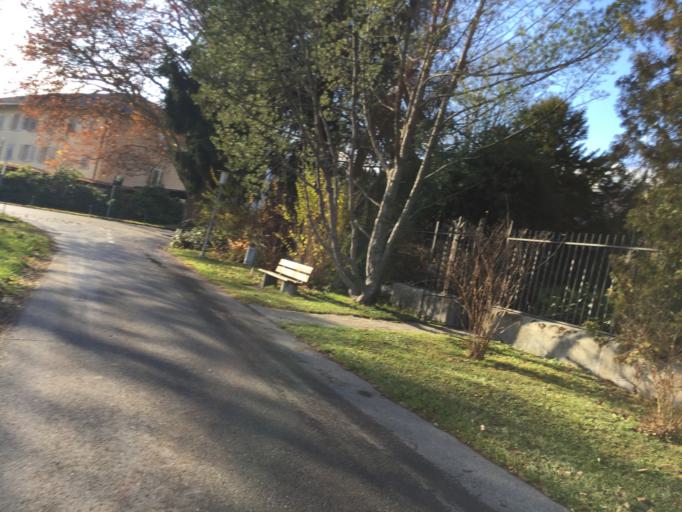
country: CH
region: Bern
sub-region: Bern-Mittelland District
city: Munsingen
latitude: 46.8791
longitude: 7.5530
